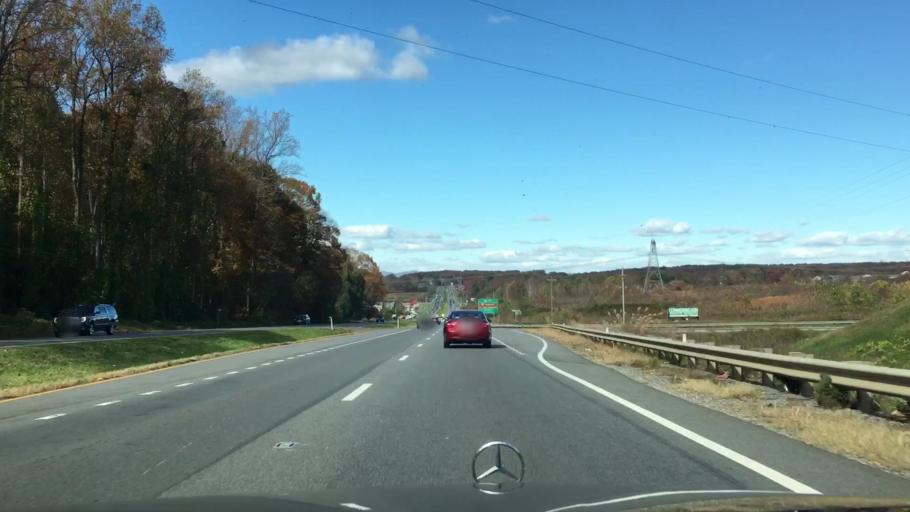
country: US
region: Virginia
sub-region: Campbell County
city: Rustburg
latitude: 37.3039
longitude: -79.1772
